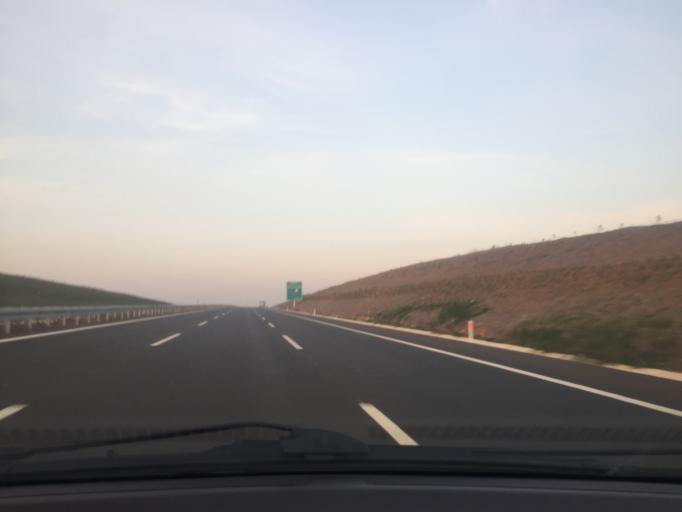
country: TR
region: Bursa
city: Mahmudiye
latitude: 40.2704
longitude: 28.6226
